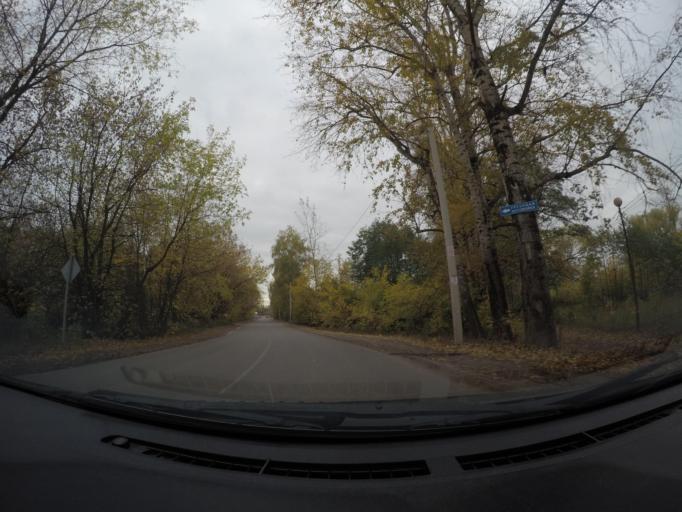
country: RU
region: Moskovskaya
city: Staraya Kupavna
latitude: 55.7970
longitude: 38.1793
